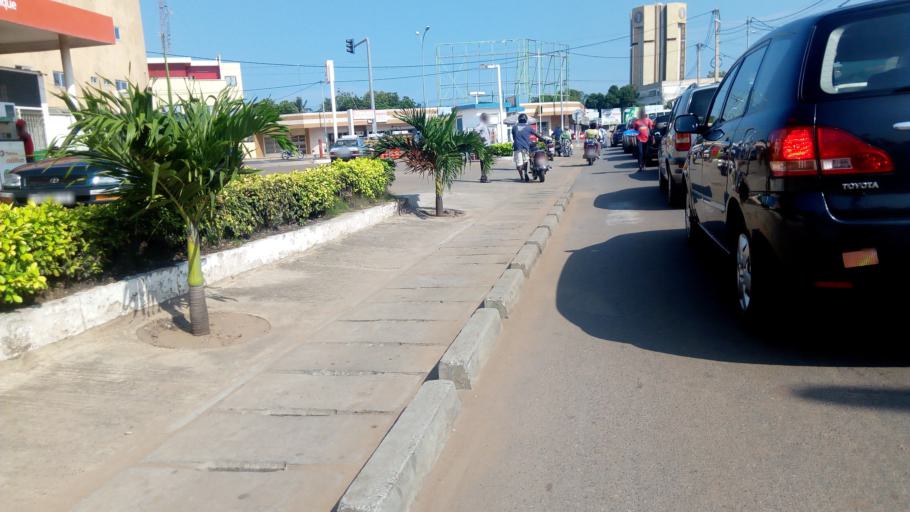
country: TG
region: Maritime
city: Lome
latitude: 6.1311
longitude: 1.2121
